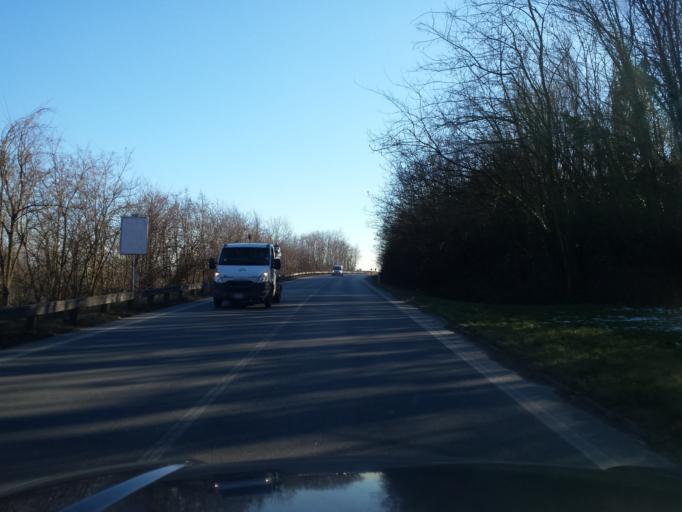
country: IT
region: Piedmont
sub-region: Provincia di Torino
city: Rivarolo Canavese
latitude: 45.3292
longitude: 7.7311
